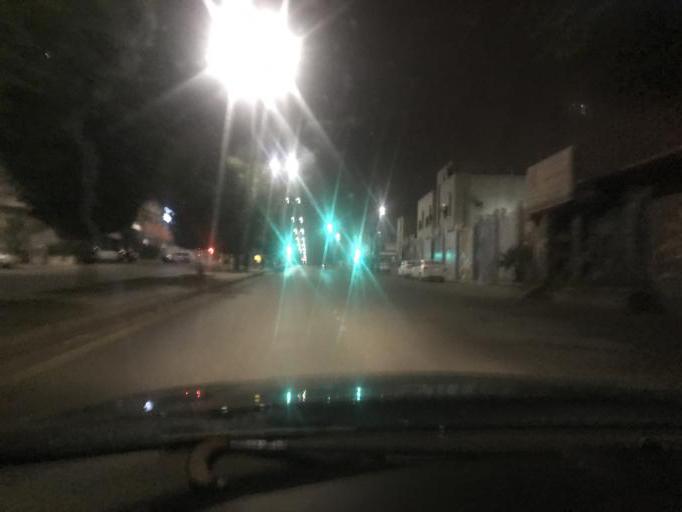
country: SA
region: Ar Riyad
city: Riyadh
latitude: 24.7302
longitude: 46.7628
